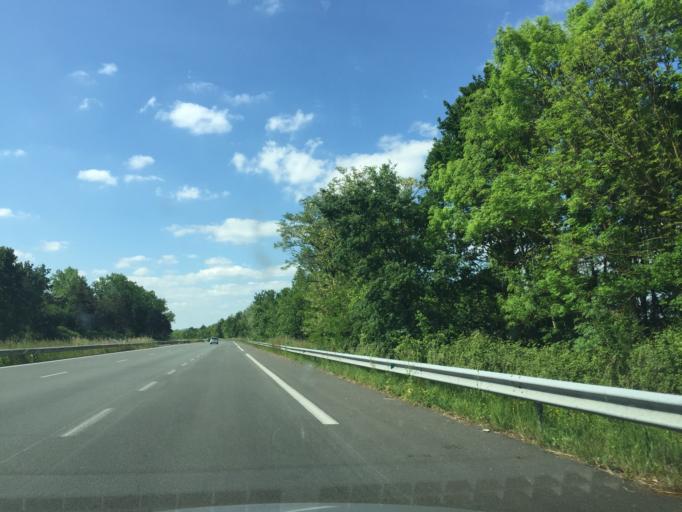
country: FR
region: Aquitaine
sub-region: Departement du Lot-et-Garonne
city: Roquefort
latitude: 44.1712
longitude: 0.5781
